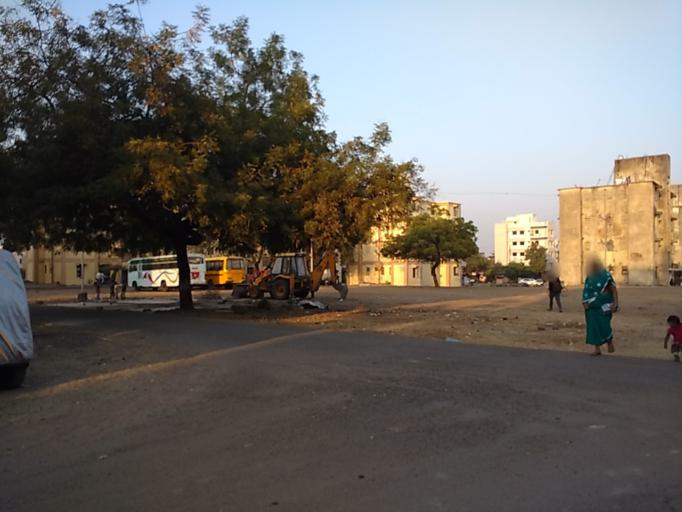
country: IN
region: Maharashtra
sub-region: Nagpur Division
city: Nagpur
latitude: 21.1796
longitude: 79.0669
